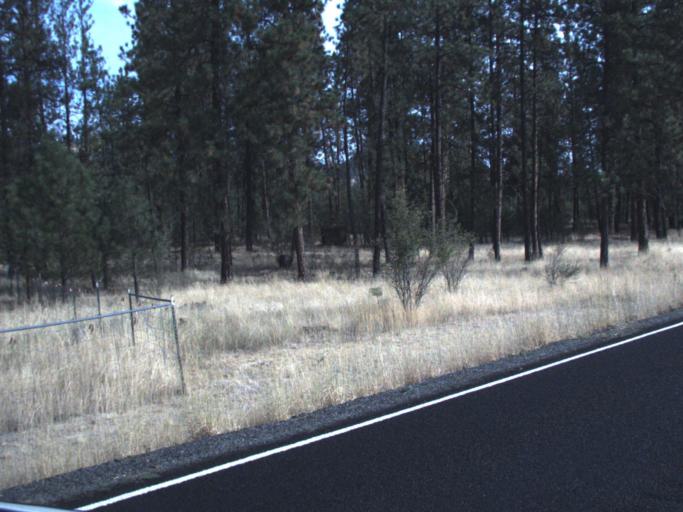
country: US
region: Washington
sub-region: Spokane County
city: Fairchild Air Force Base
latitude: 47.8449
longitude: -117.7326
